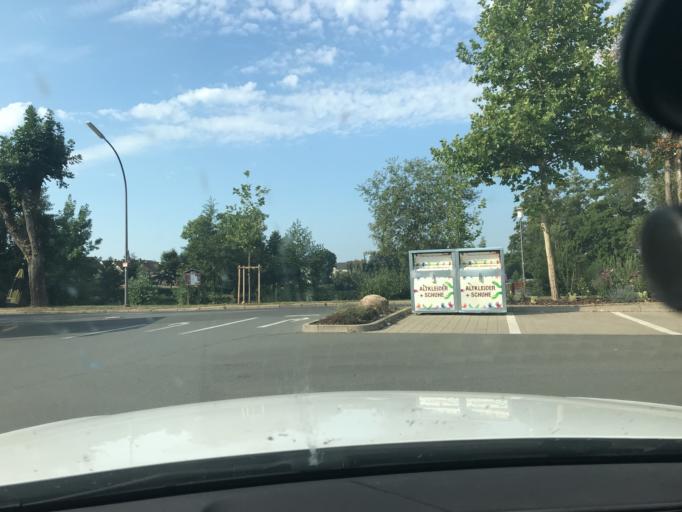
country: DE
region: Bavaria
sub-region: Upper Palatinate
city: Auerbach
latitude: 49.6959
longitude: 11.6248
